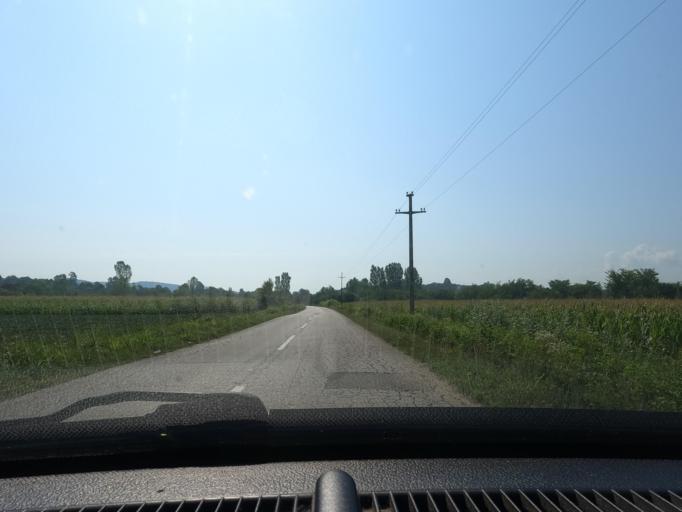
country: RS
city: Kozjak
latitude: 44.5734
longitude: 19.2794
